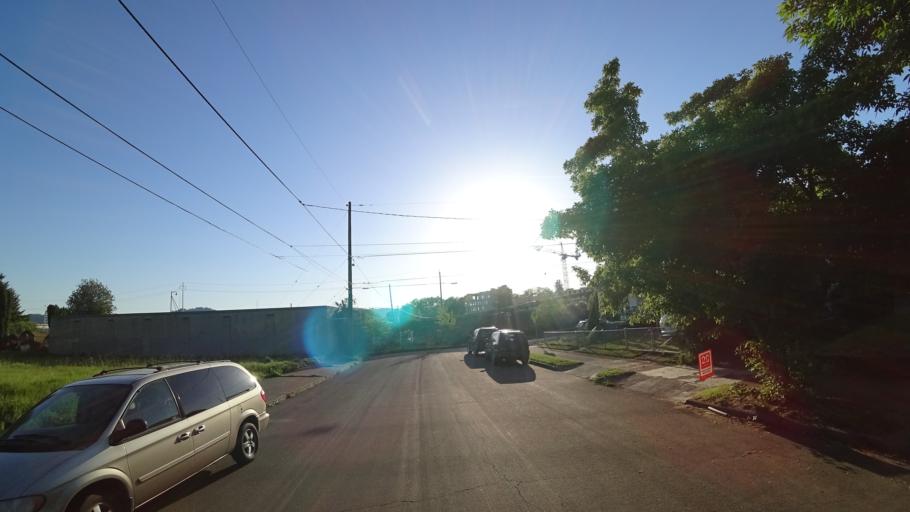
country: US
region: Oregon
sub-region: Multnomah County
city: Portland
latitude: 45.5463
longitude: -122.6729
